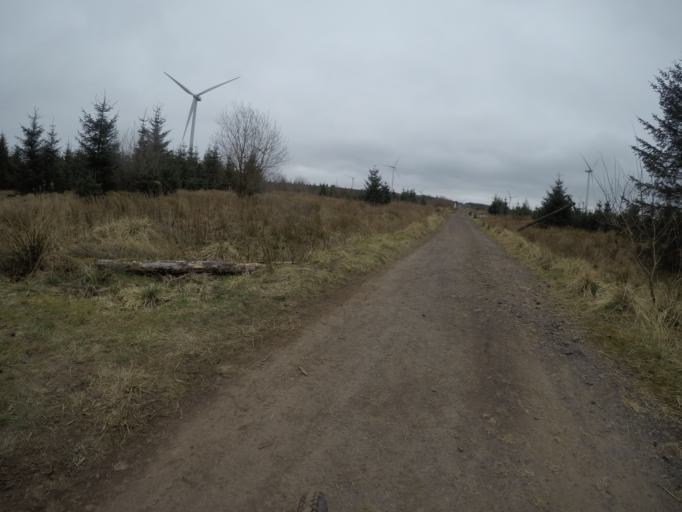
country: GB
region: Scotland
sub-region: East Ayrshire
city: Newmilns
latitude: 55.6581
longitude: -4.3316
